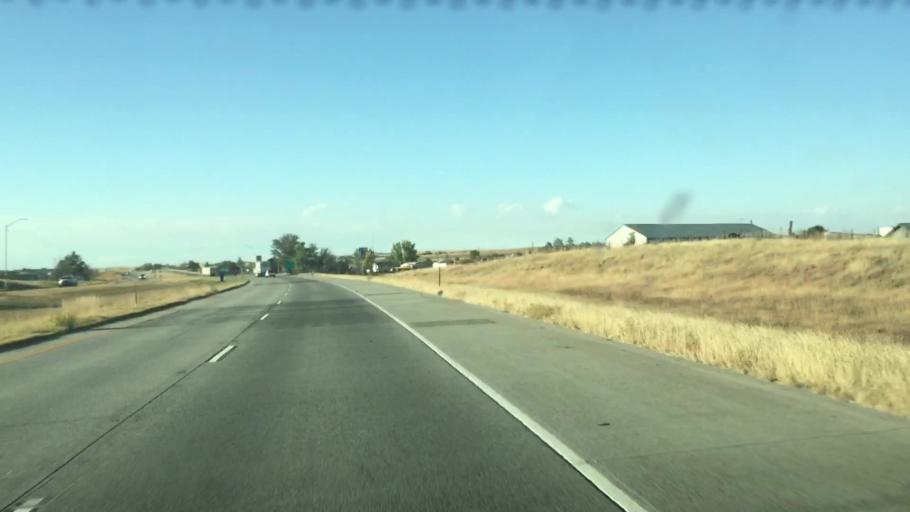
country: US
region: Colorado
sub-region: Arapahoe County
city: Byers
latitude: 39.6090
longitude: -104.0372
